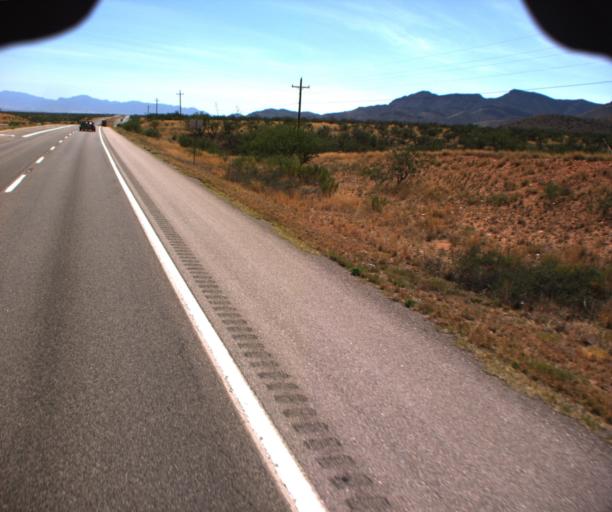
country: US
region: Arizona
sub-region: Cochise County
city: Whetstone
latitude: 31.8465
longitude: -110.3417
